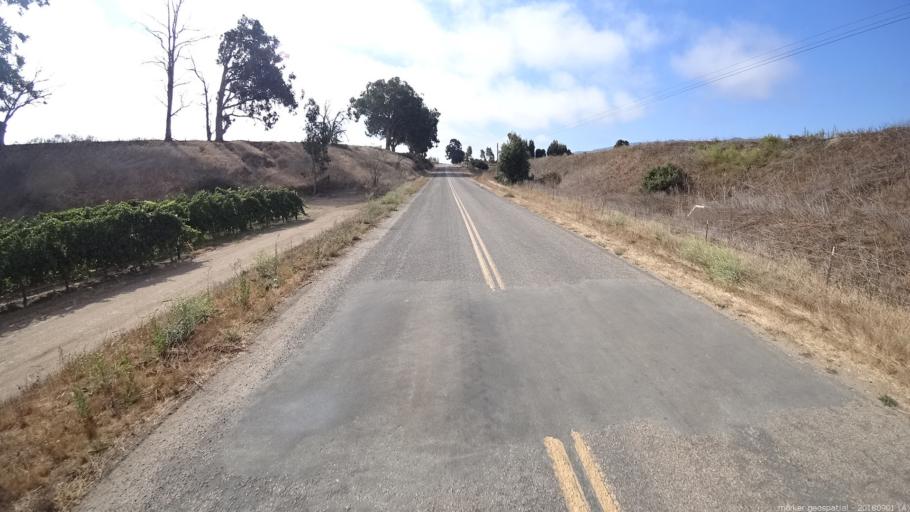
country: US
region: California
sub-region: Monterey County
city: Soledad
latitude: 36.3743
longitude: -121.3375
